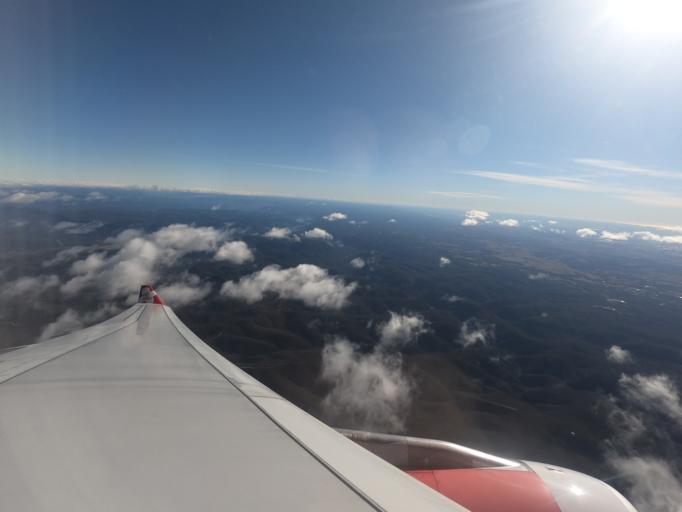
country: AU
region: New South Wales
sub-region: Wollondilly
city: Buxton
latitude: -34.2707
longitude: 150.4341
